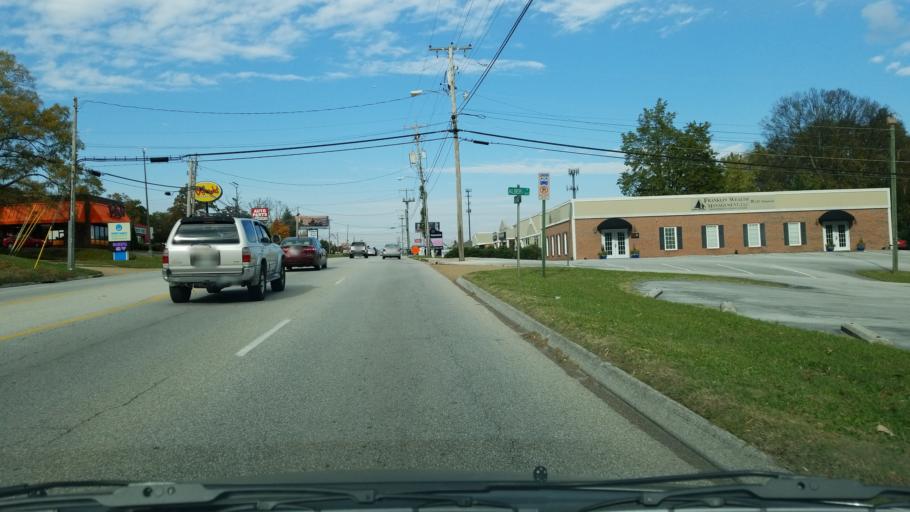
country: US
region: Tennessee
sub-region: Hamilton County
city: Red Bank
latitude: 35.1234
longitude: -85.2480
